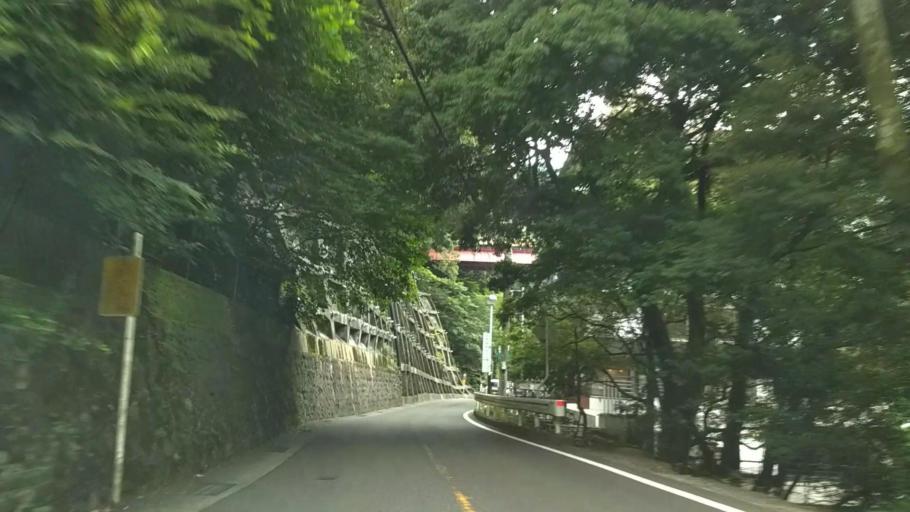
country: JP
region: Kanagawa
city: Odawara
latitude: 35.2276
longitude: 139.0950
